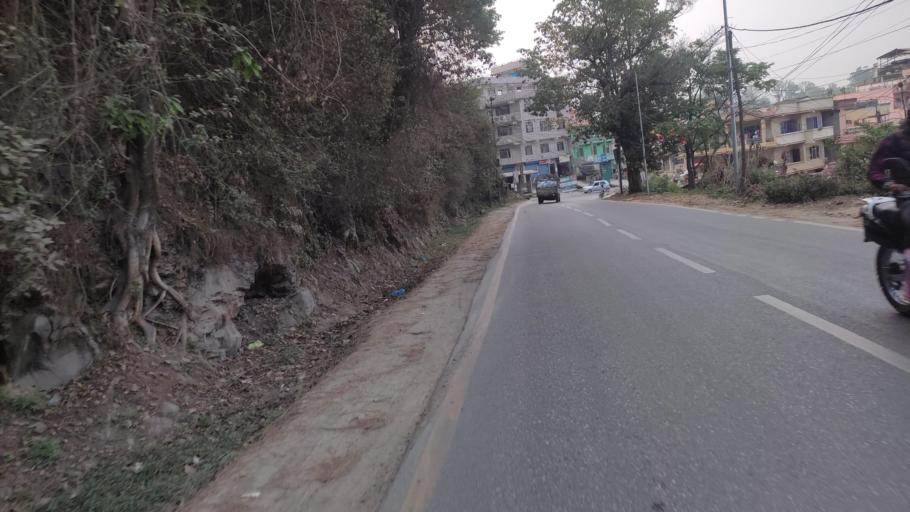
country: NP
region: Central Region
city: Kirtipur
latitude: 27.6697
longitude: 85.2908
